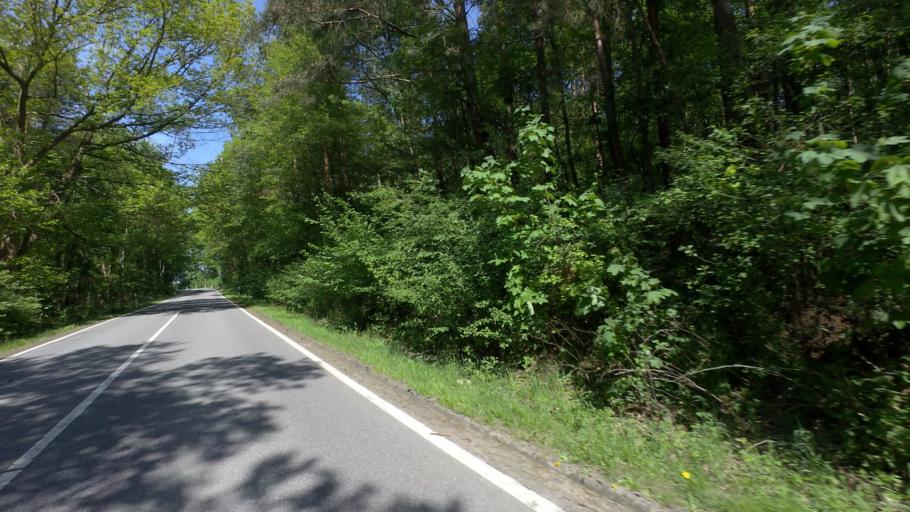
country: DE
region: Mecklenburg-Vorpommern
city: Mollenhagen
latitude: 53.5736
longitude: 12.8955
